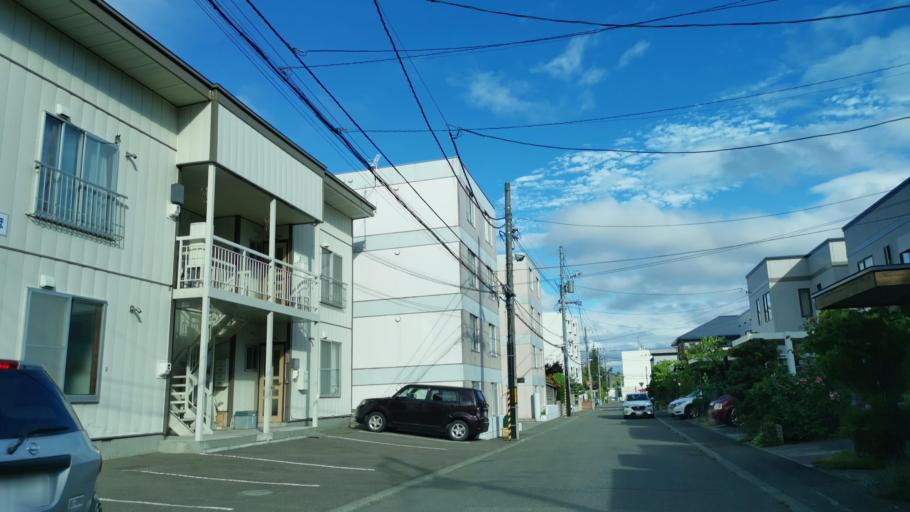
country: JP
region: Hokkaido
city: Sapporo
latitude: 43.0633
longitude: 141.2962
